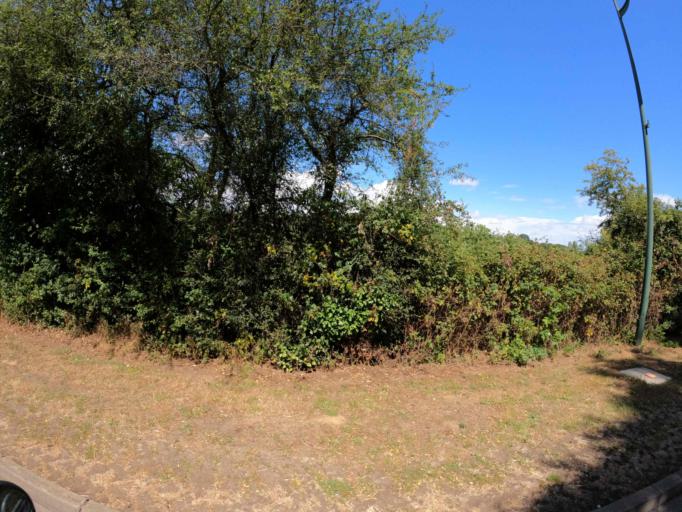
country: FR
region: Pays de la Loire
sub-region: Departement de la Sarthe
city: Brulon
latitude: 47.9205
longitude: -0.2664
